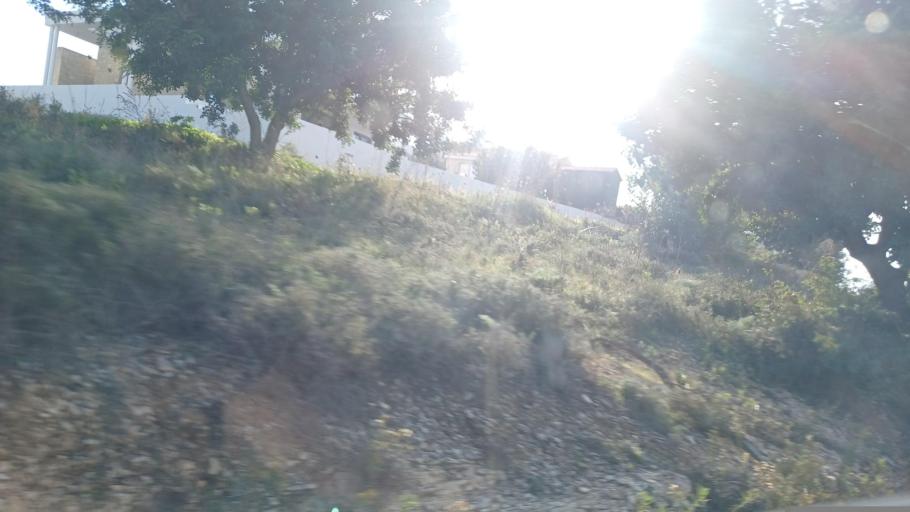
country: CY
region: Pafos
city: Mesogi
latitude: 34.7997
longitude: 32.4878
